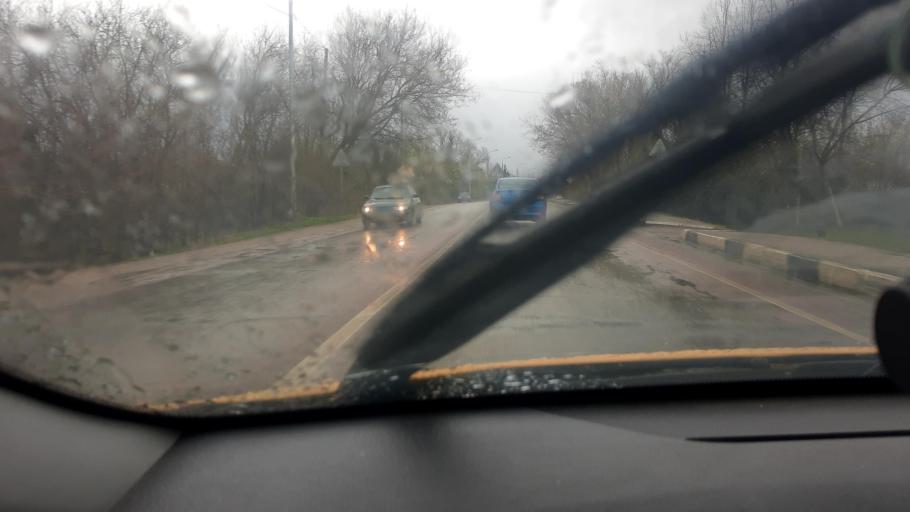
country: RU
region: Moskovskaya
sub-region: Volokolamskiy Rayon
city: Volokolamsk
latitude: 55.9957
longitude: 35.9238
